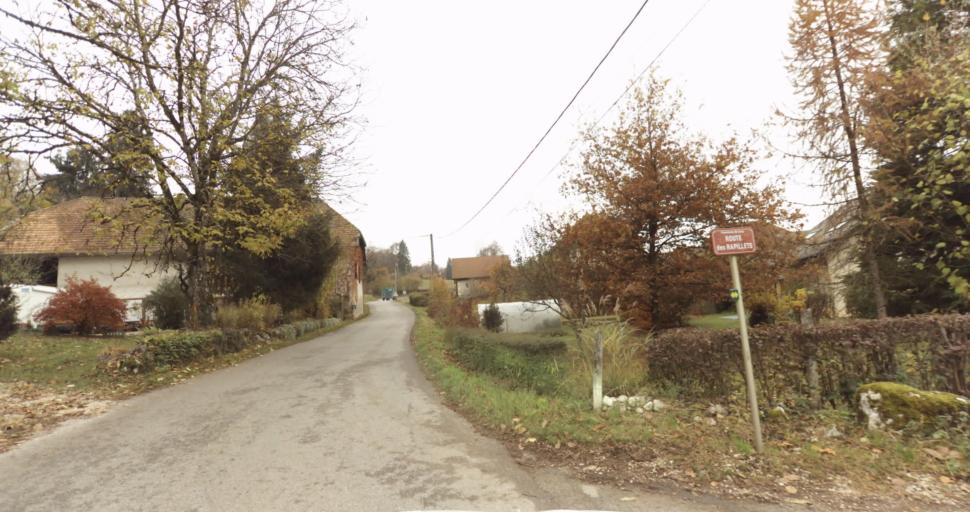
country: FR
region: Rhone-Alpes
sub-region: Departement de la Haute-Savoie
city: Cusy
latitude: 45.7516
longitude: 6.0161
